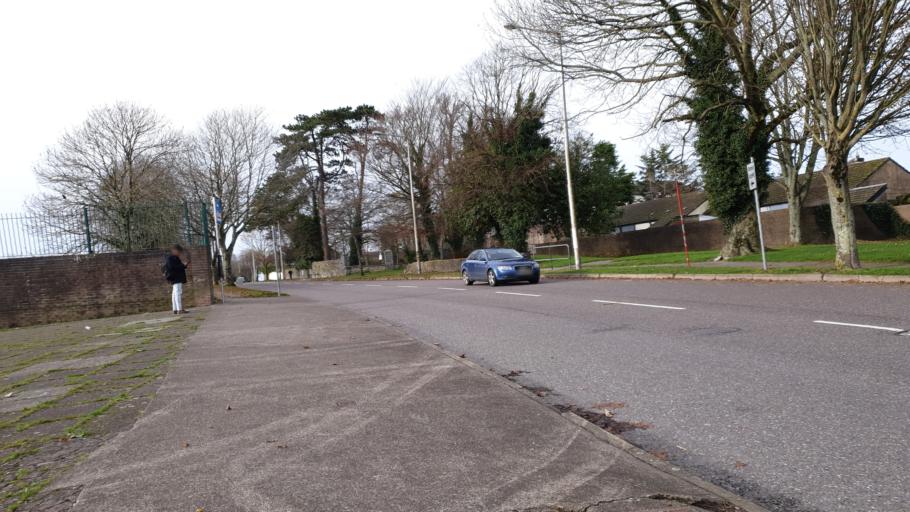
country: IE
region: Munster
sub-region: County Cork
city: Passage West
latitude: 51.8949
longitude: -8.4007
